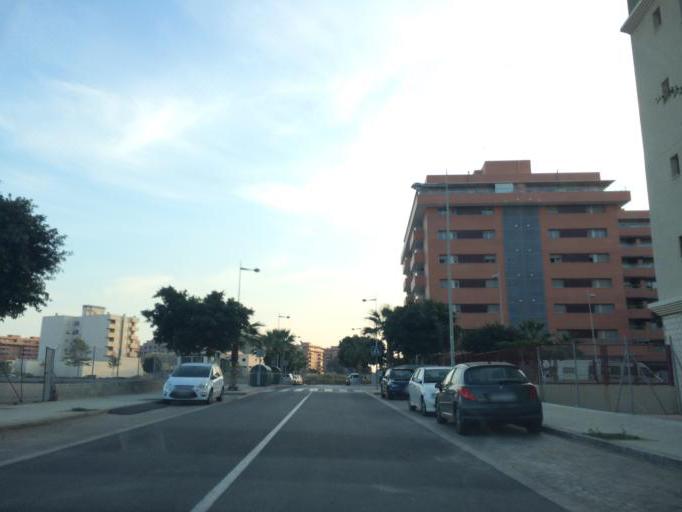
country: ES
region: Andalusia
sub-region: Provincia de Almeria
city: Almeria
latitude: 36.8352
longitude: -2.4400
